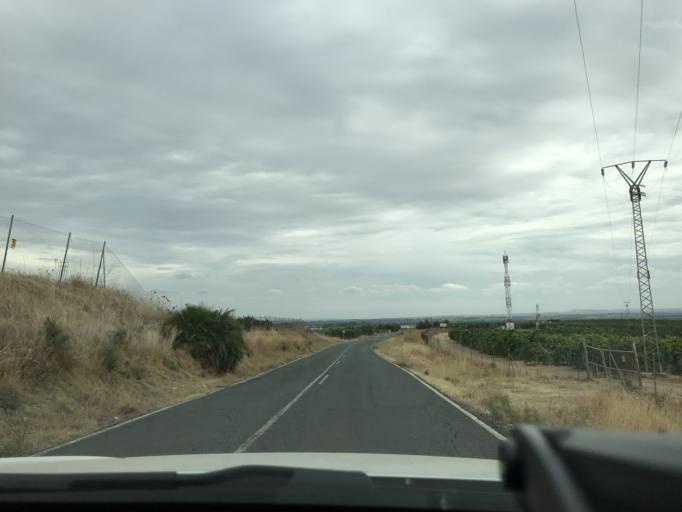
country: ES
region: Andalusia
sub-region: Provincia de Sevilla
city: Villanueva del Rio y Minas
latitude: 37.6412
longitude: -5.7048
